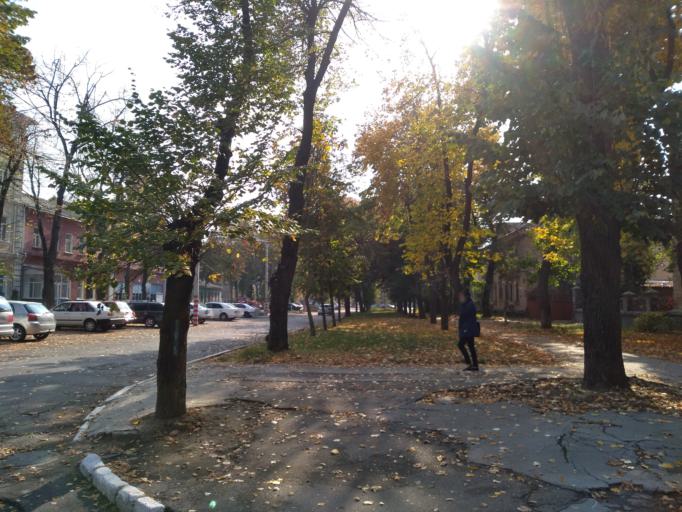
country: MD
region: Bender
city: Bender
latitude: 46.8213
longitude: 29.4810
